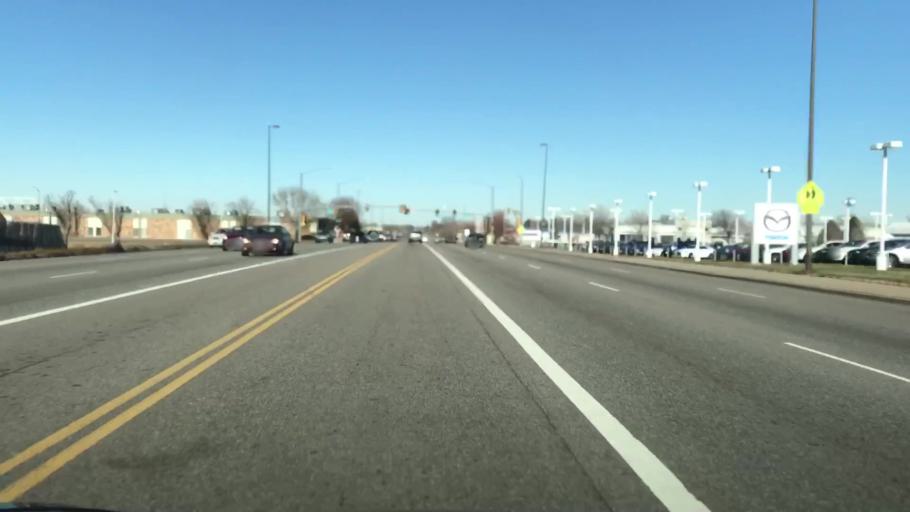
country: US
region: Colorado
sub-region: Adams County
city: Aurora
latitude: 39.7168
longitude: -104.8660
